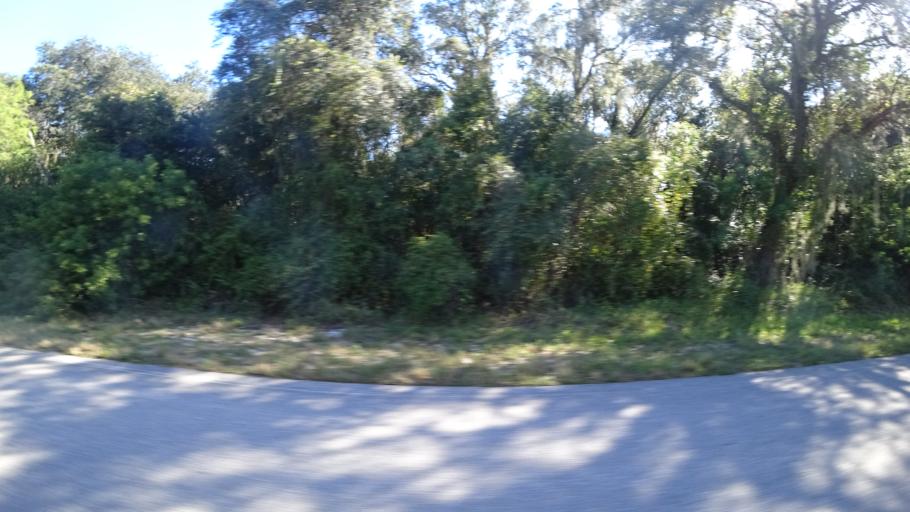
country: US
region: Florida
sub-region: Hillsborough County
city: Wimauma
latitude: 27.6437
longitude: -82.2925
